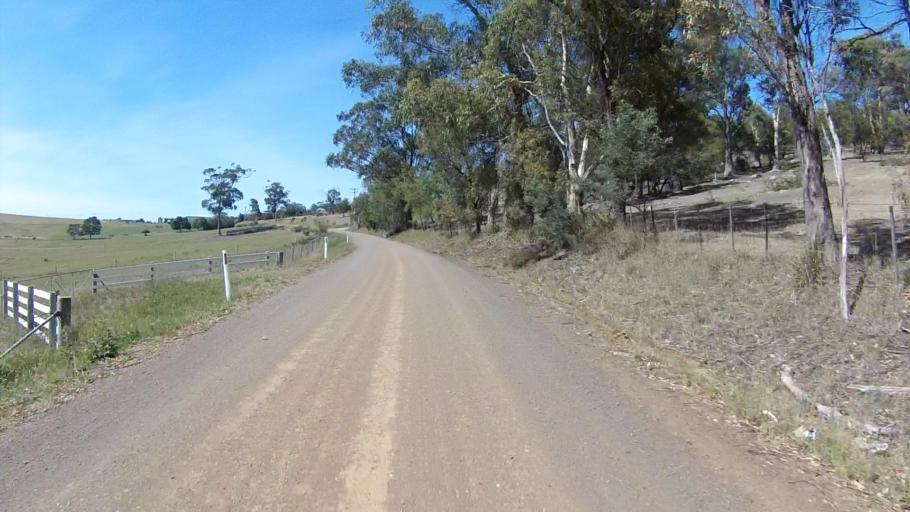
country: AU
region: Tasmania
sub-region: Sorell
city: Sorell
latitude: -42.7383
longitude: 147.5982
